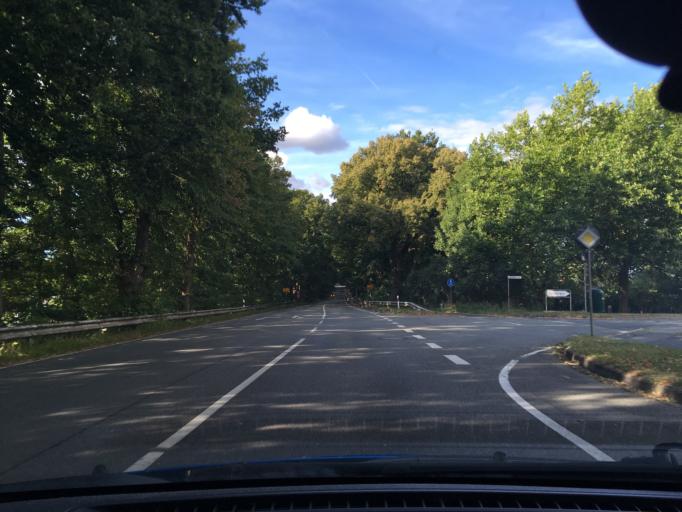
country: DE
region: Lower Saxony
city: Seevetal
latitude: 53.4064
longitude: 9.9254
